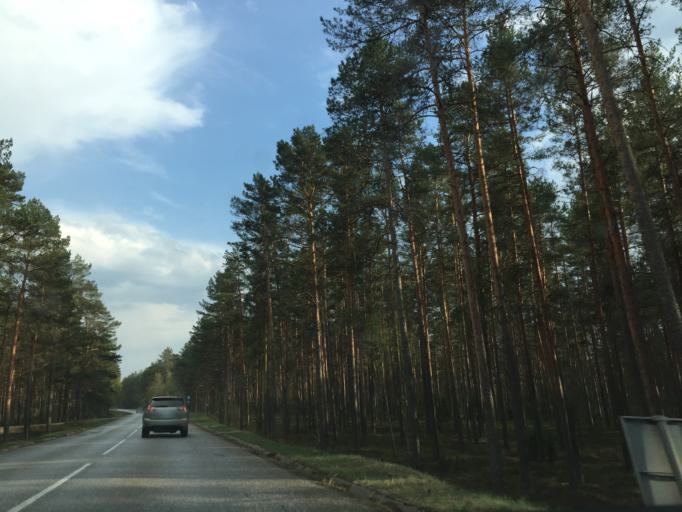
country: LV
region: Garkalne
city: Garkalne
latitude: 57.0375
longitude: 24.4169
